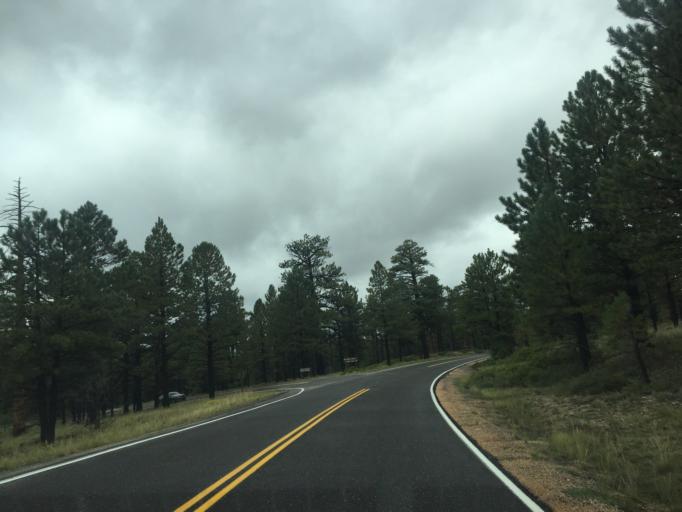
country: US
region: Utah
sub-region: Garfield County
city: Panguitch
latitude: 37.6007
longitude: -112.1647
